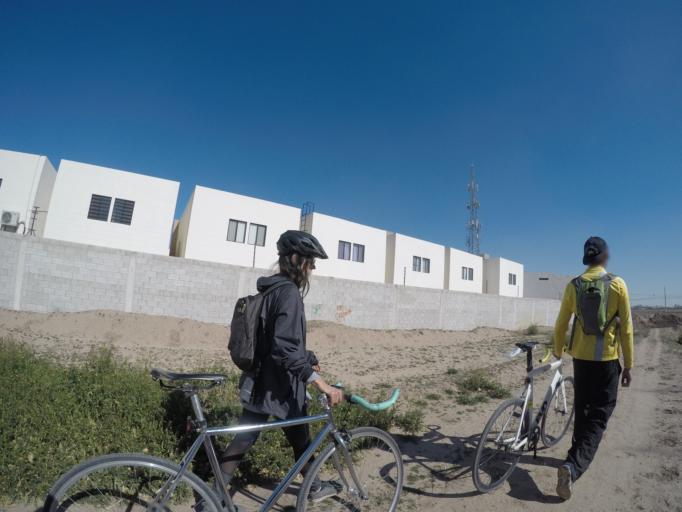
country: US
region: Texas
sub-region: El Paso County
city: Socorro
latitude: 31.6606
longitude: -106.3734
